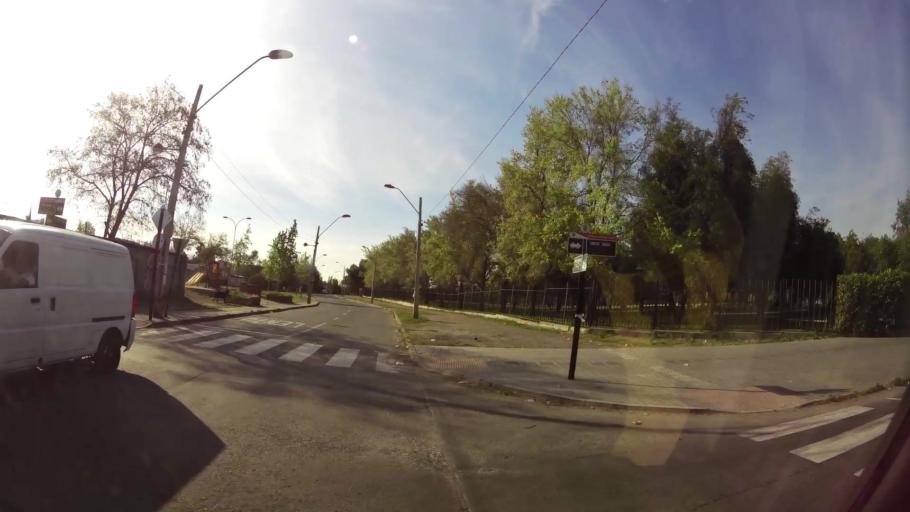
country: CL
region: Santiago Metropolitan
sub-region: Provincia de Santiago
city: Santiago
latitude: -33.5124
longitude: -70.6298
